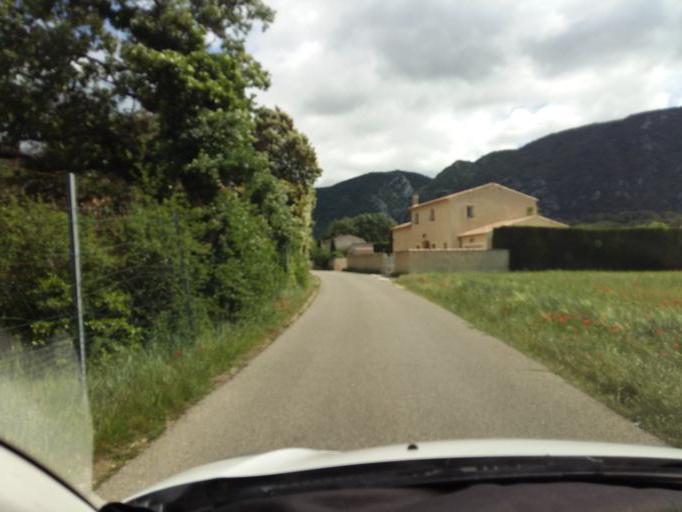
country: FR
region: Provence-Alpes-Cote d'Azur
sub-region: Departement du Vaucluse
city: Maubec
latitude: 43.8452
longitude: 5.1358
